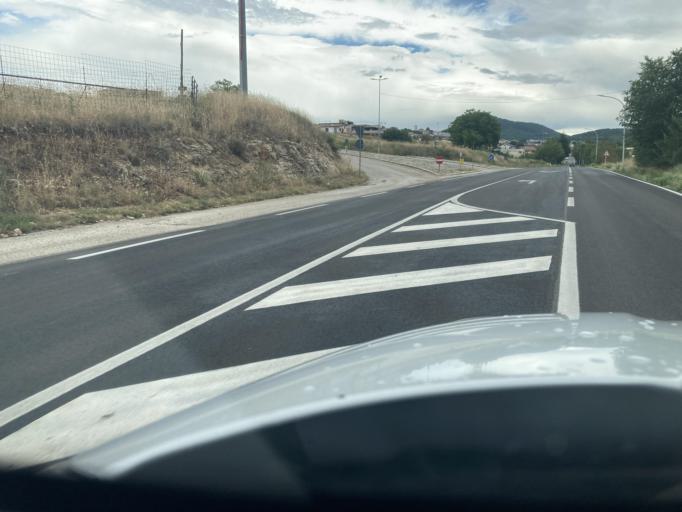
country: IT
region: Abruzzo
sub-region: Provincia dell' Aquila
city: San Demetrio Ne' Vestini
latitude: 42.2932
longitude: 13.5411
